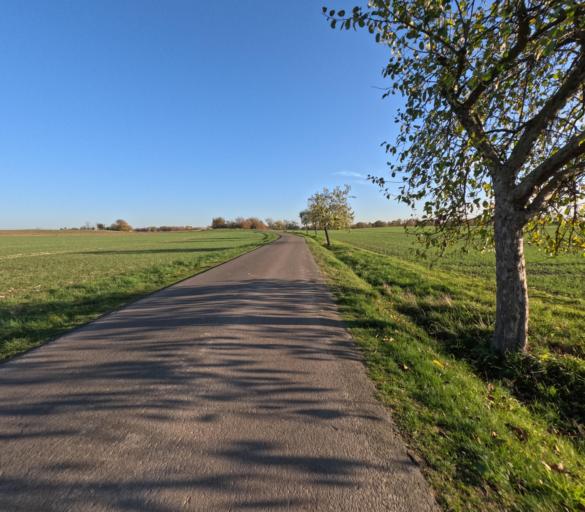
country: DE
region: Saxony
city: Grossbardau
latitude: 51.2449
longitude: 12.6702
